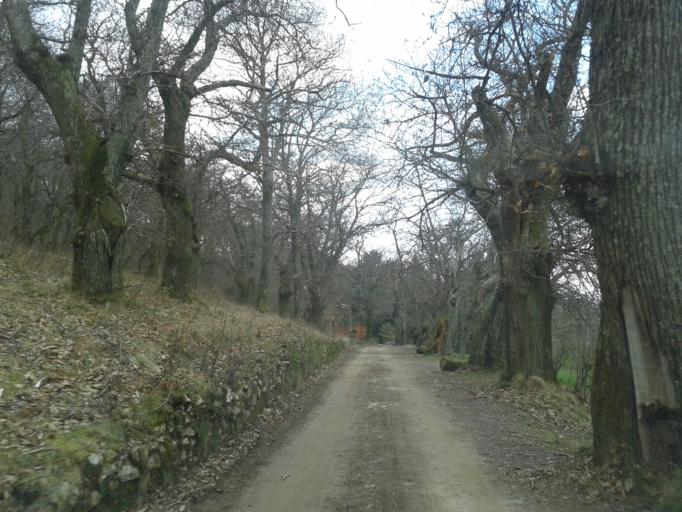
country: IT
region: Tuscany
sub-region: Province of Pisa
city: Calci
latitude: 43.7652
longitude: 10.5266
